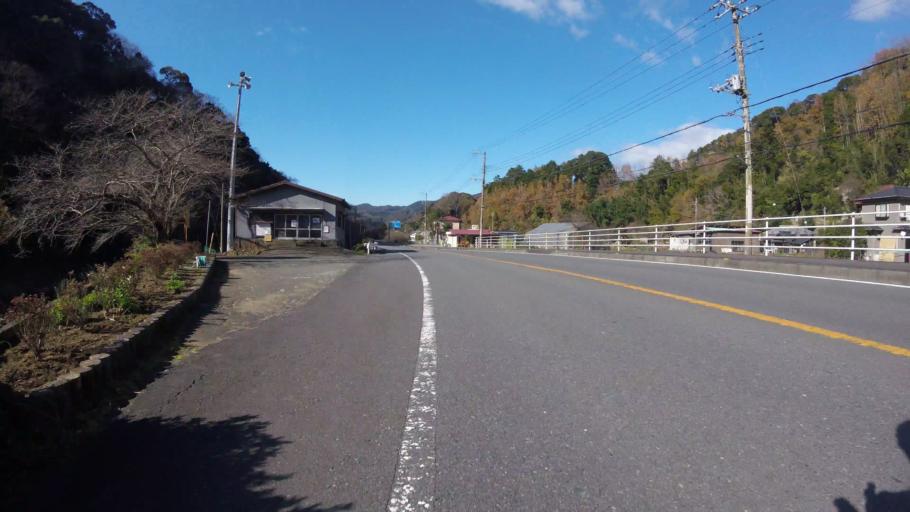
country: JP
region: Shizuoka
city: Shimoda
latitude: 34.7550
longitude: 138.8302
